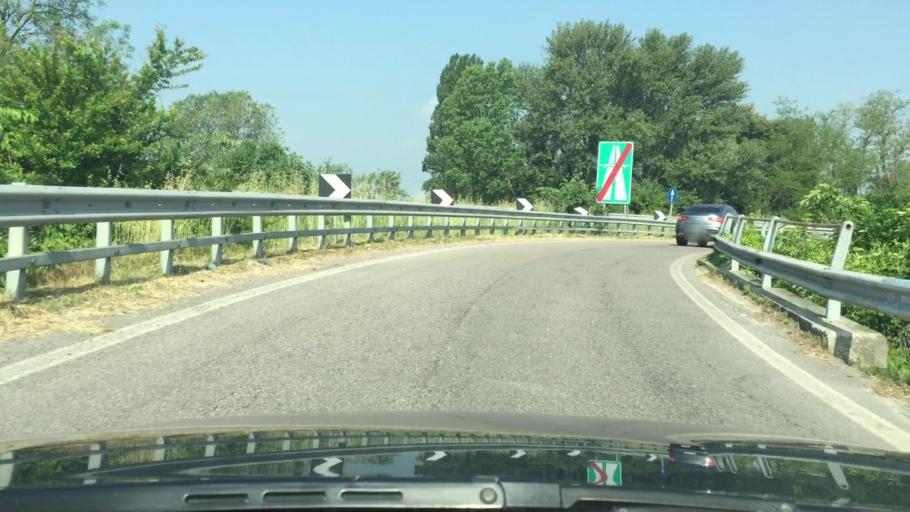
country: IT
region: Emilia-Romagna
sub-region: Provincia di Ferrara
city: Gaibanella-Sant'Edigio
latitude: 44.7963
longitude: 11.6377
